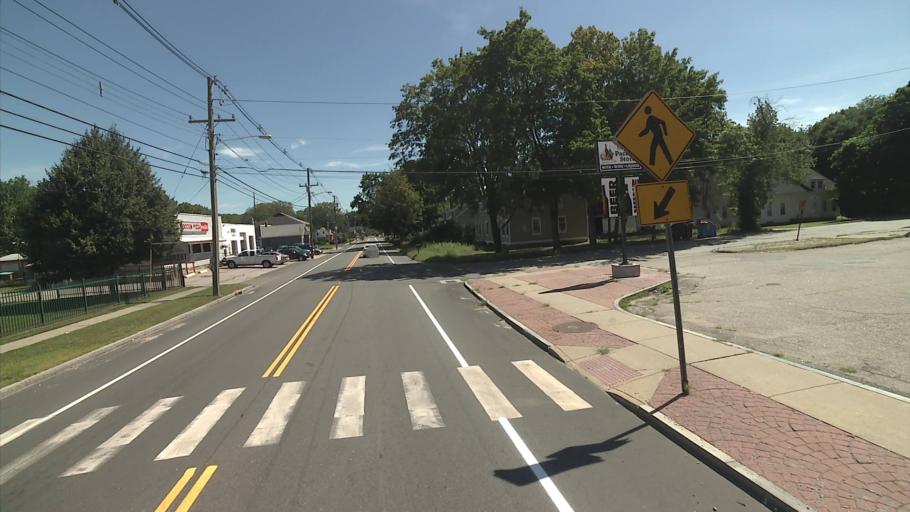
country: US
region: Connecticut
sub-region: New London County
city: Lisbon
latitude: 41.5945
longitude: -72.0497
